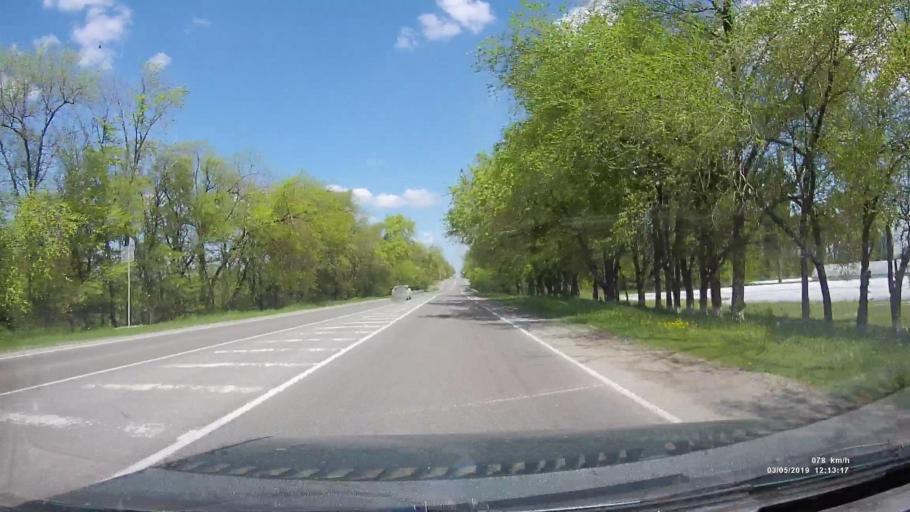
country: RU
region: Rostov
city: Melikhovskaya
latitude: 47.3310
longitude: 40.5537
